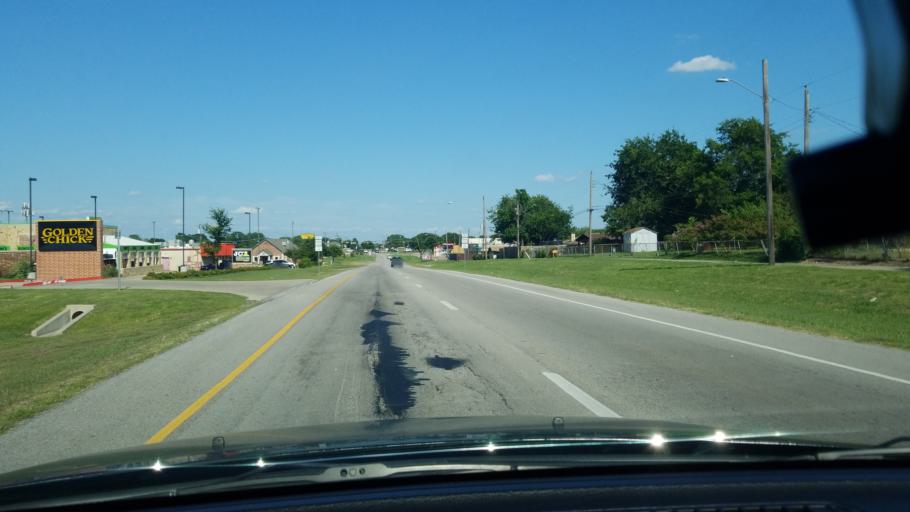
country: US
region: Texas
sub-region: Dallas County
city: Mesquite
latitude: 32.7652
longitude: -96.5867
